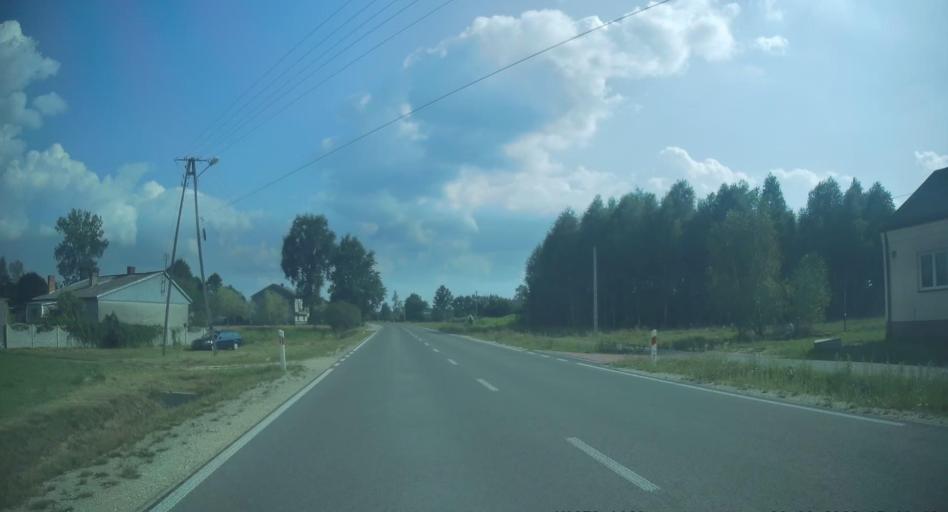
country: PL
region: Swietokrzyskie
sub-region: Powiat konecki
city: Radoszyce
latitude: 51.0562
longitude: 20.2790
